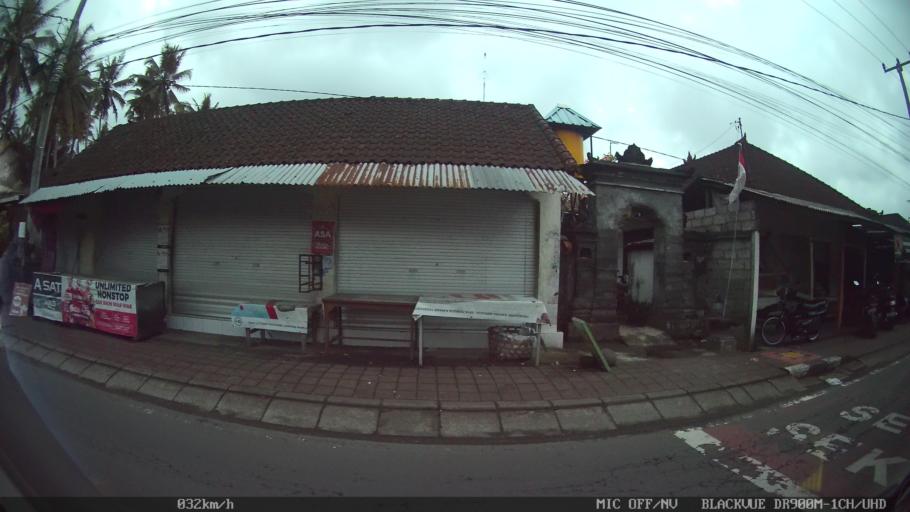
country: ID
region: Bali
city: Banjar Cemenggon
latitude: -8.5410
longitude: 115.2057
